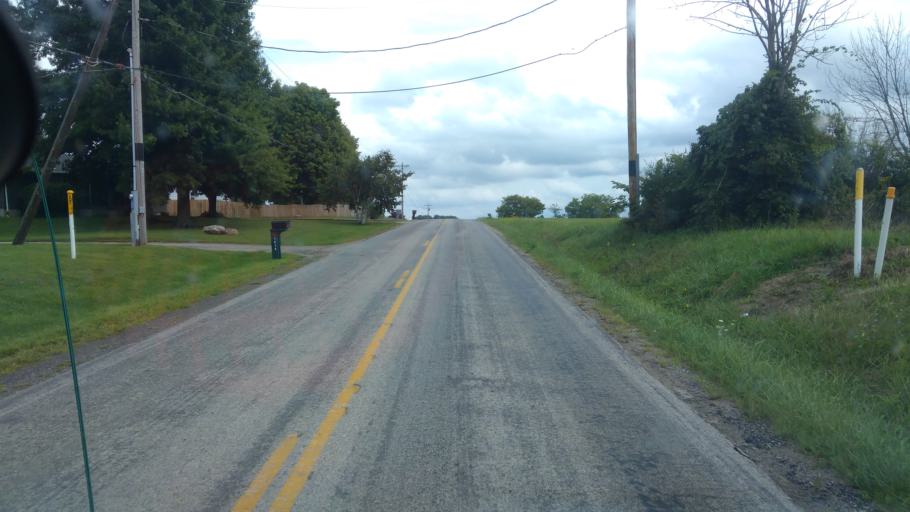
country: US
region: Ohio
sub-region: Ashland County
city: Ashland
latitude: 40.8513
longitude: -82.3976
